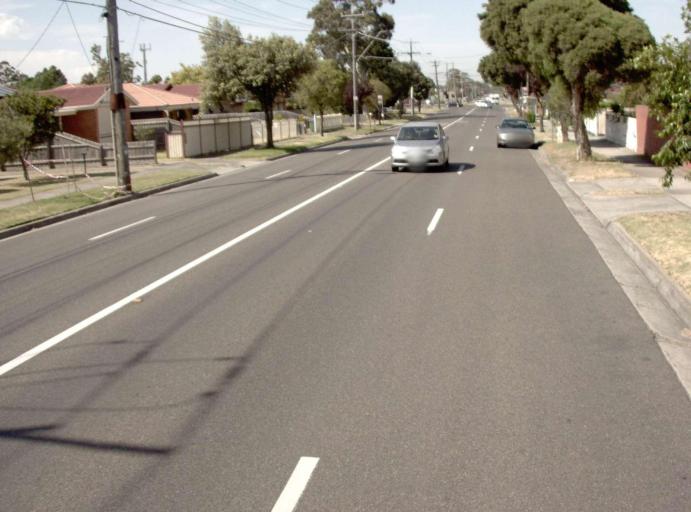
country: AU
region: Victoria
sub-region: Greater Dandenong
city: Keysborough
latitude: -37.9930
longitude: 145.1821
